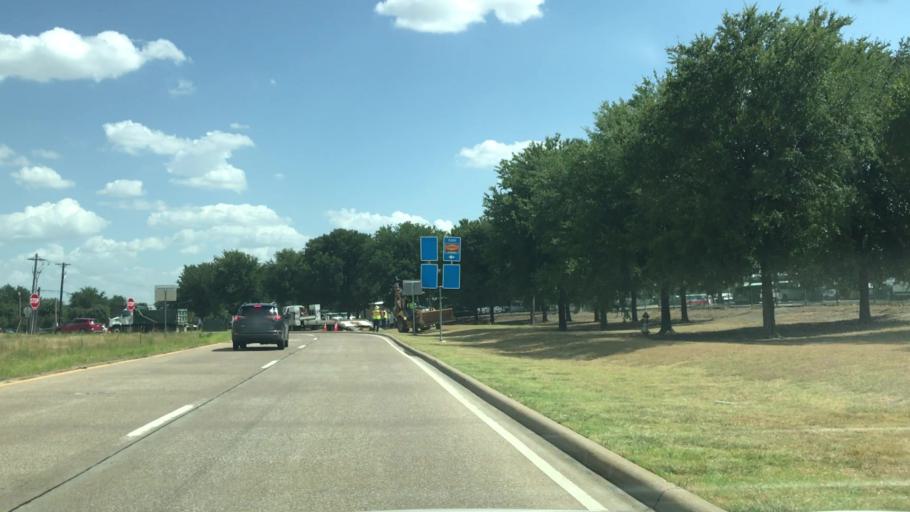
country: US
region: Texas
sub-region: Dallas County
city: Coppell
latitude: 32.9146
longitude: -97.0086
